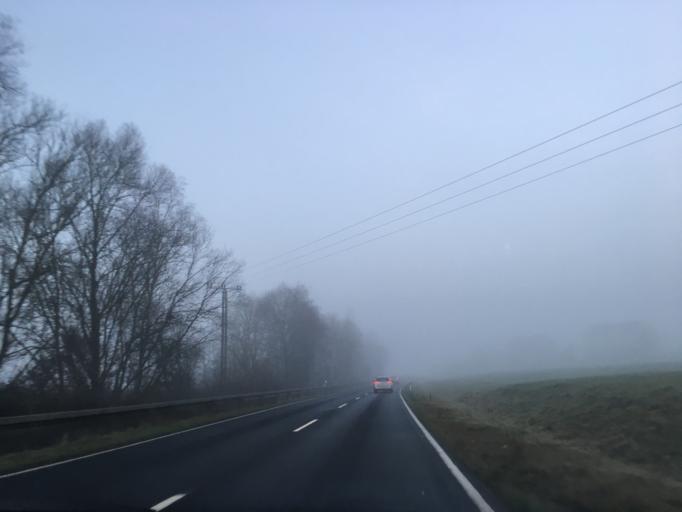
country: DE
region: Hesse
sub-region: Regierungsbezirk Kassel
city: Petersberg
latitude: 50.5642
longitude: 9.7467
